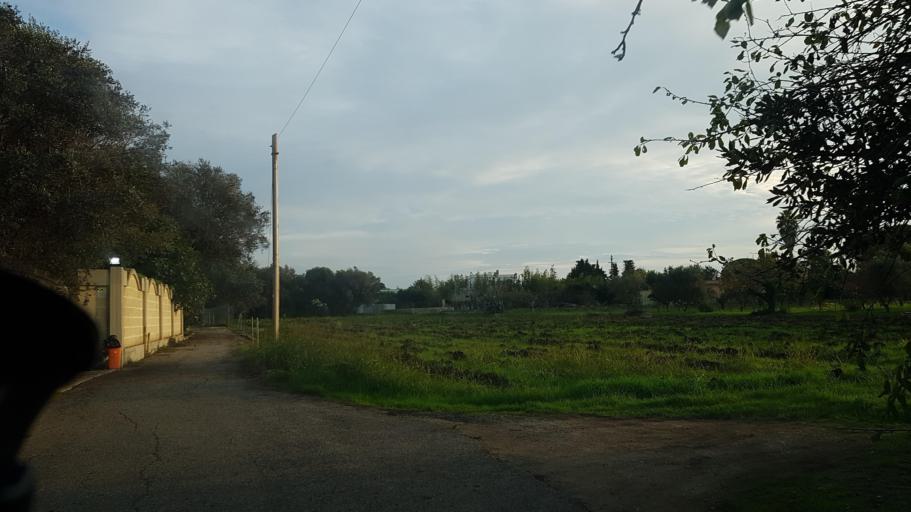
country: IT
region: Apulia
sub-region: Provincia di Brindisi
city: Latiano
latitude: 40.5566
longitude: 17.7310
